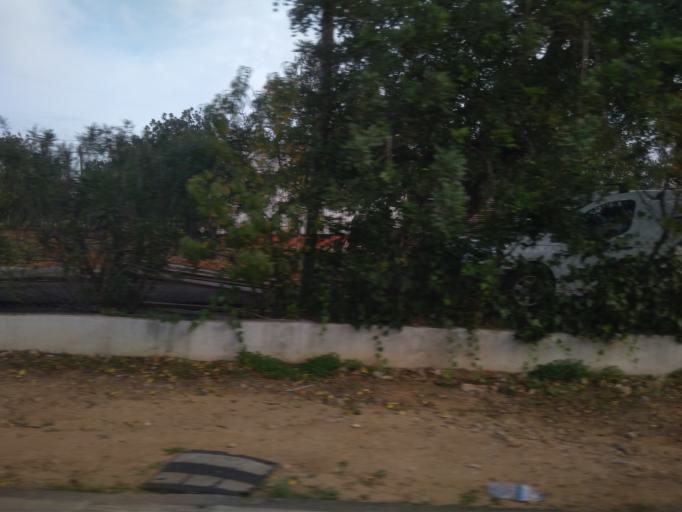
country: PT
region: Faro
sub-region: Faro
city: Santa Barbara de Nexe
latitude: 37.0784
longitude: -7.9593
